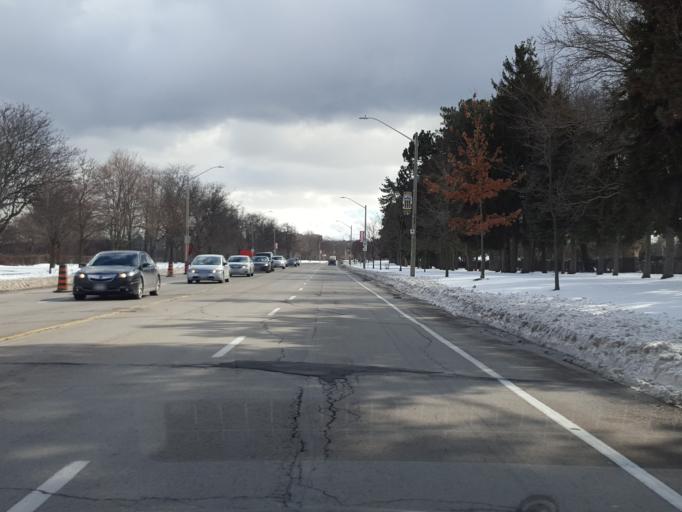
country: CA
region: Ontario
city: Hamilton
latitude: 43.2766
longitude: -79.8896
